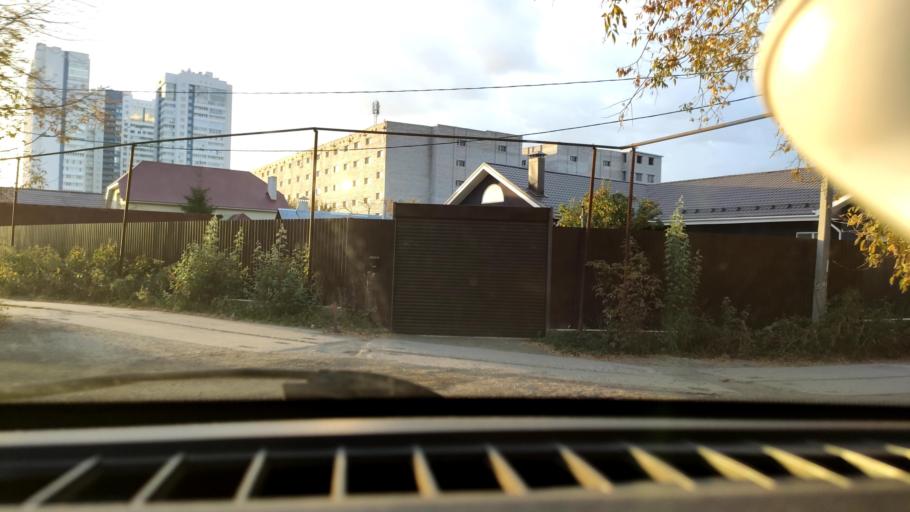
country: RU
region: Samara
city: Samara
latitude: 53.2689
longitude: 50.2290
